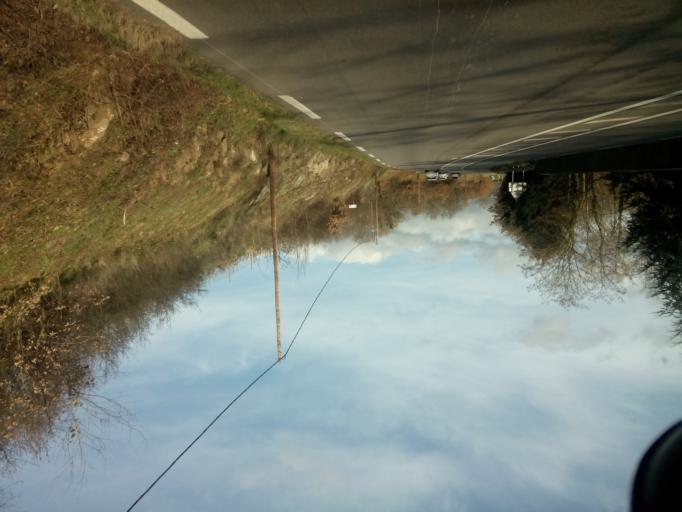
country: FR
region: Rhone-Alpes
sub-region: Departement de l'Ardeche
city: Serrieres
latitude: 45.3091
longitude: 4.7503
